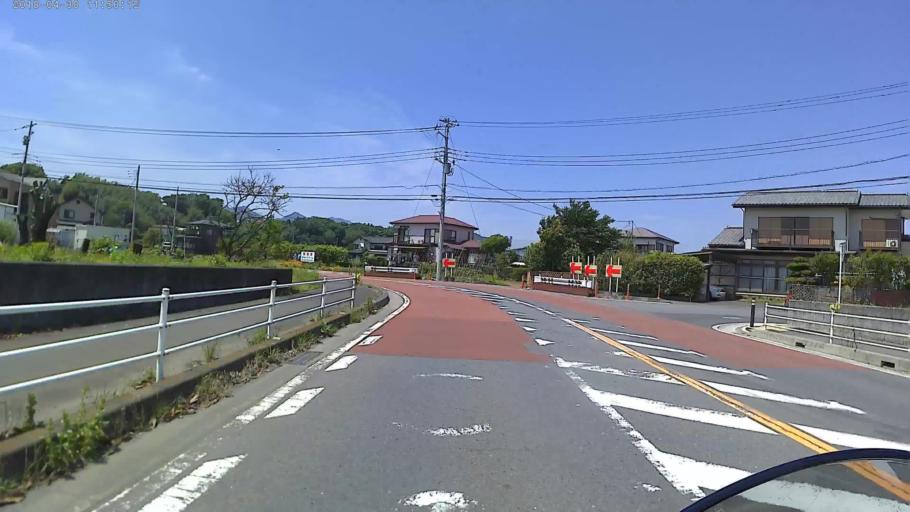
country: JP
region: Kanagawa
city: Zama
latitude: 35.4847
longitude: 139.3514
